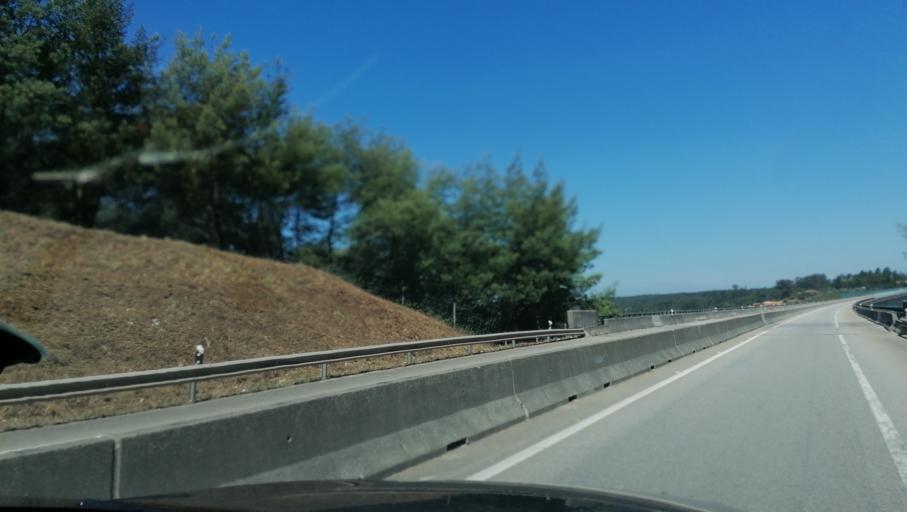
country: PT
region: Aveiro
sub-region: Agueda
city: Agueda
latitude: 40.5674
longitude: -8.4758
